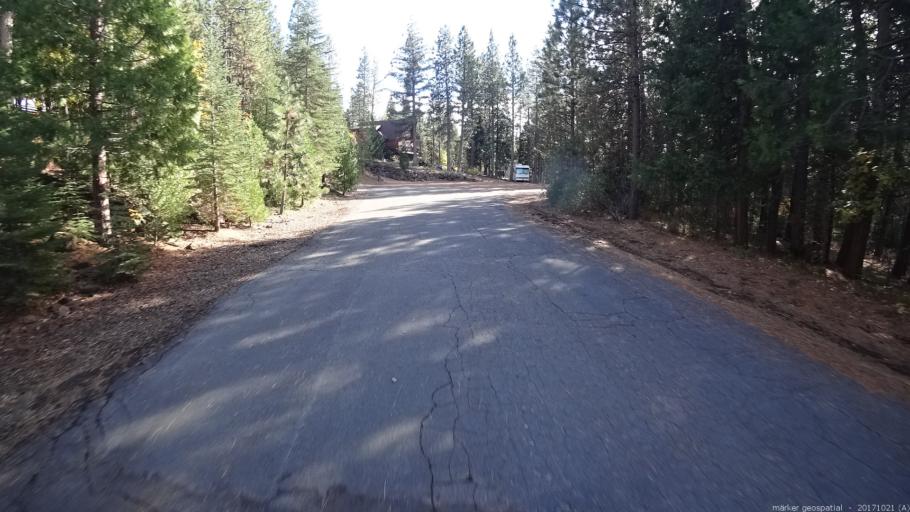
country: US
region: California
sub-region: Shasta County
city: Burney
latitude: 40.8711
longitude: -121.6624
